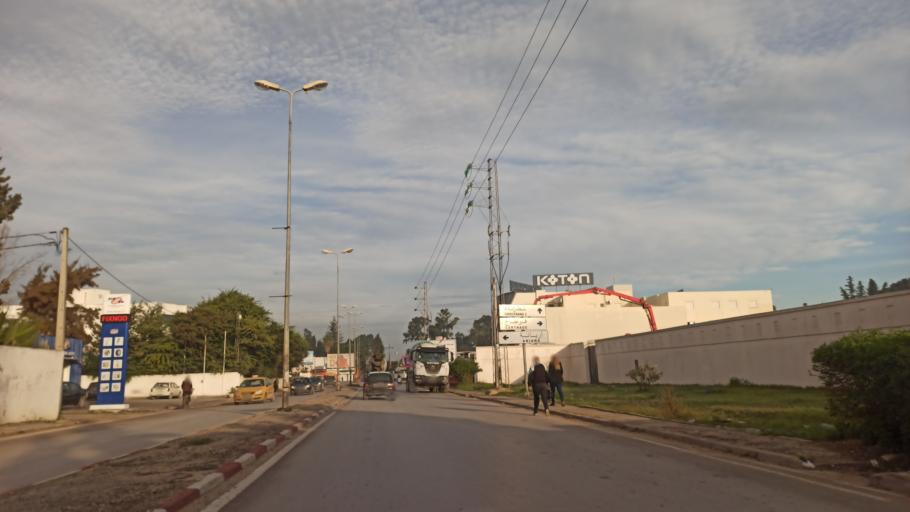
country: TN
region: Ariana
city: Ariana
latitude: 36.8738
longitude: 10.2465
